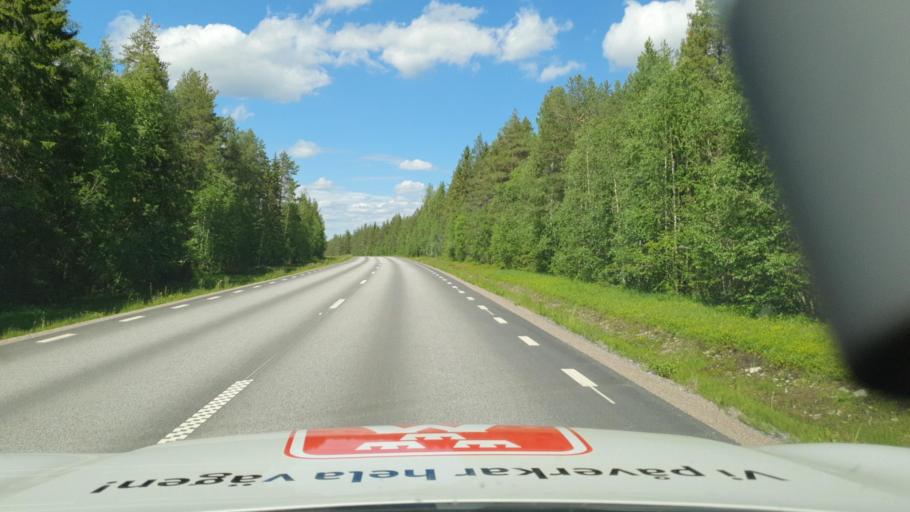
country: SE
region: Vaesterbotten
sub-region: Skelleftea Kommun
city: Boliden
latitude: 64.9145
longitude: 20.3394
